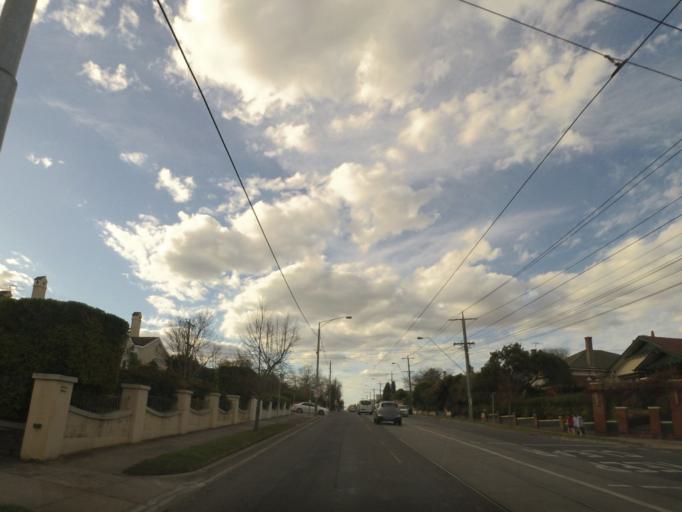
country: AU
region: Victoria
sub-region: Stonnington
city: Glen Iris
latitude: -37.8485
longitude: 145.0533
